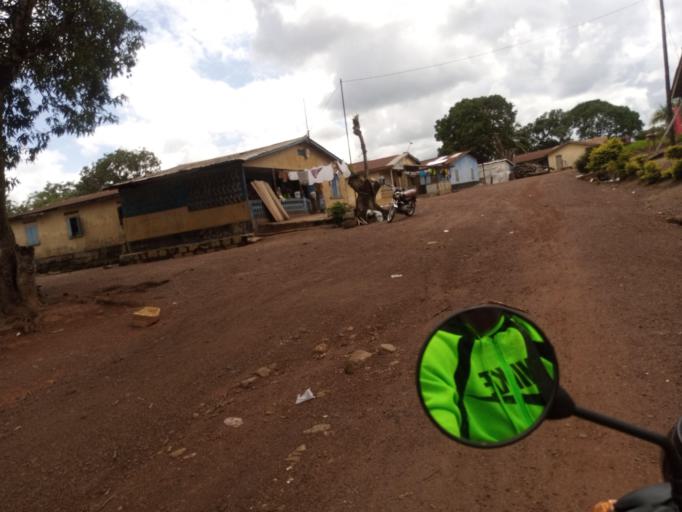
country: SL
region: Northern Province
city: Port Loko
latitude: 8.7616
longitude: -12.7818
